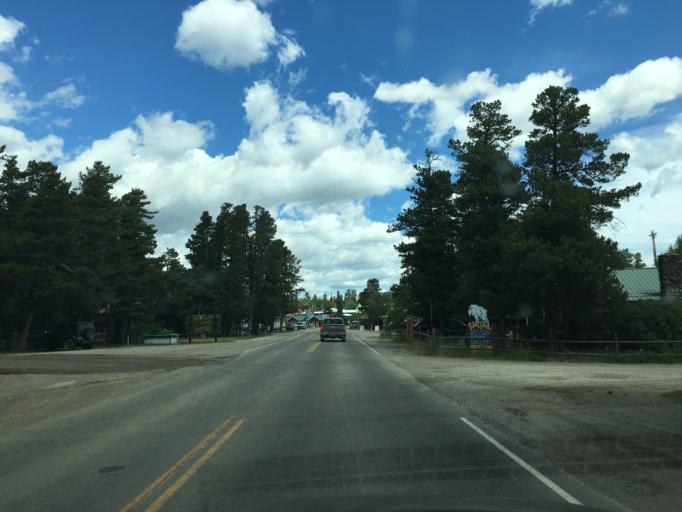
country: US
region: Montana
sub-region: Glacier County
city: South Browning
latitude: 48.4472
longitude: -113.2246
